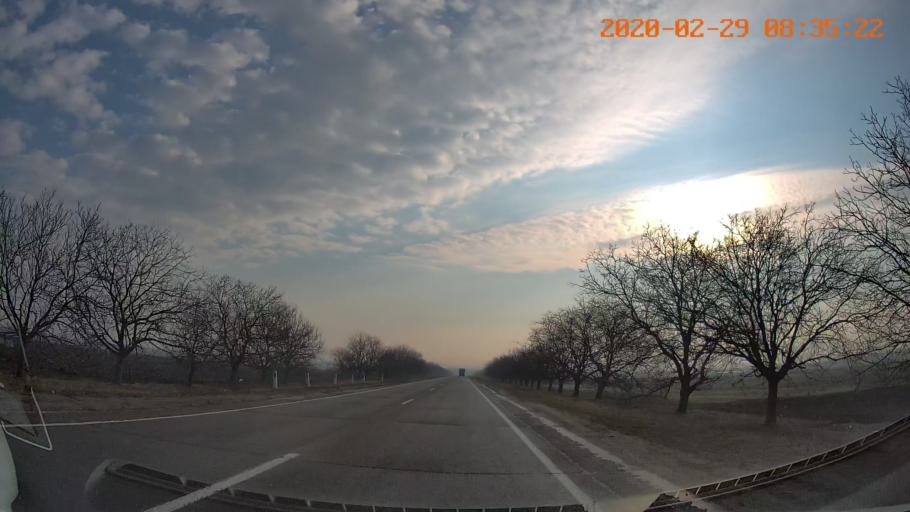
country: MD
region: Anenii Noi
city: Anenii Noi
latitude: 46.9228
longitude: 29.3262
